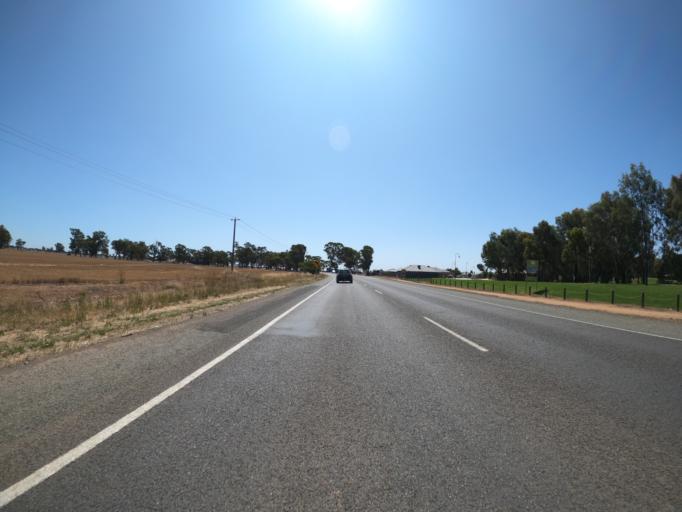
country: AU
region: Victoria
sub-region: Moira
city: Yarrawonga
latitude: -36.0111
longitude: 146.0342
